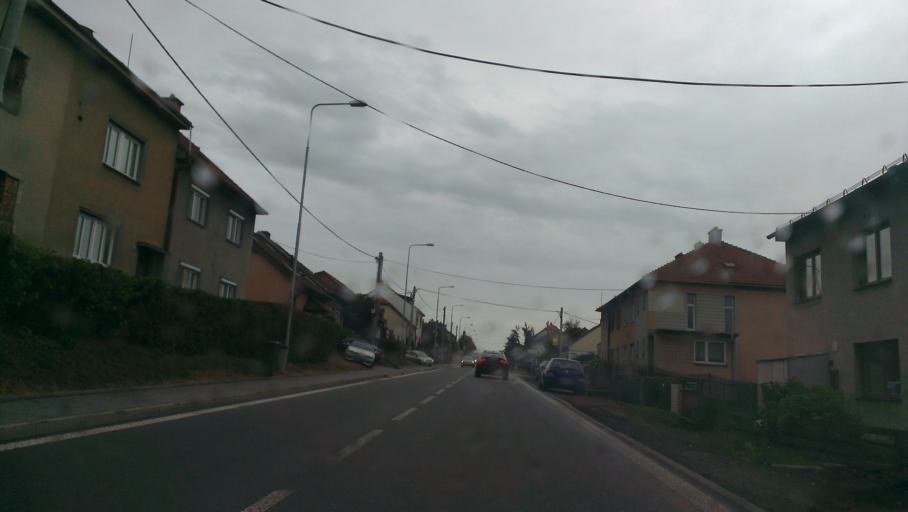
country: CZ
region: Vysocina
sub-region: Okres Zd'ar nad Sazavou
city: Velke Mezirici
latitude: 49.3487
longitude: 16.0285
